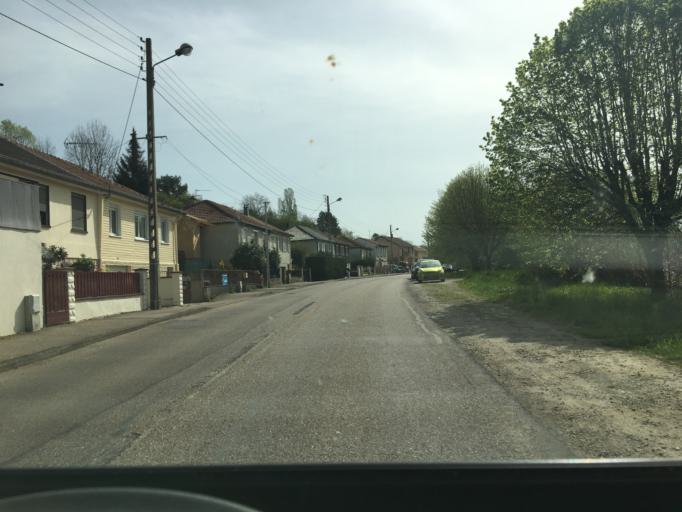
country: FR
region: Lorraine
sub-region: Departement de Meurthe-et-Moselle
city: Chaligny
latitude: 48.6205
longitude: 6.0826
